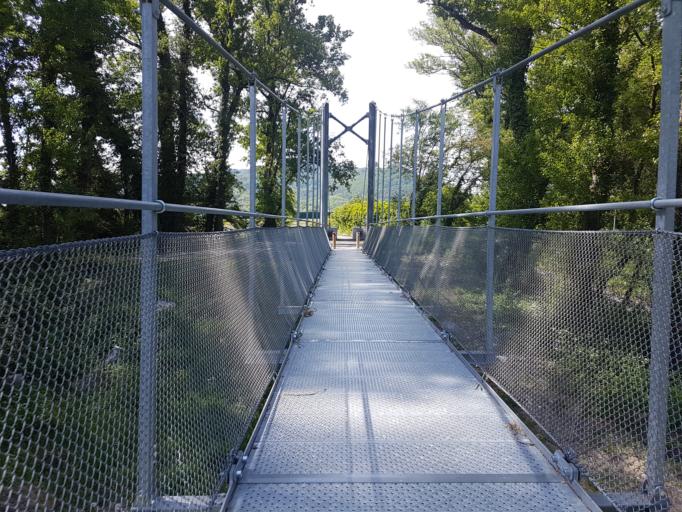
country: FR
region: Rhone-Alpes
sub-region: Departement de l'Ardeche
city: Le Pouzin
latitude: 44.7306
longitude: 4.7571
